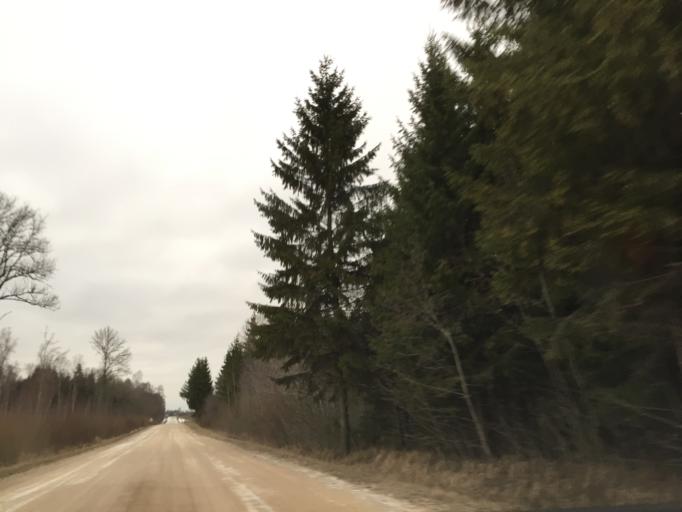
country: LT
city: Zagare
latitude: 56.3005
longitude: 23.2616
